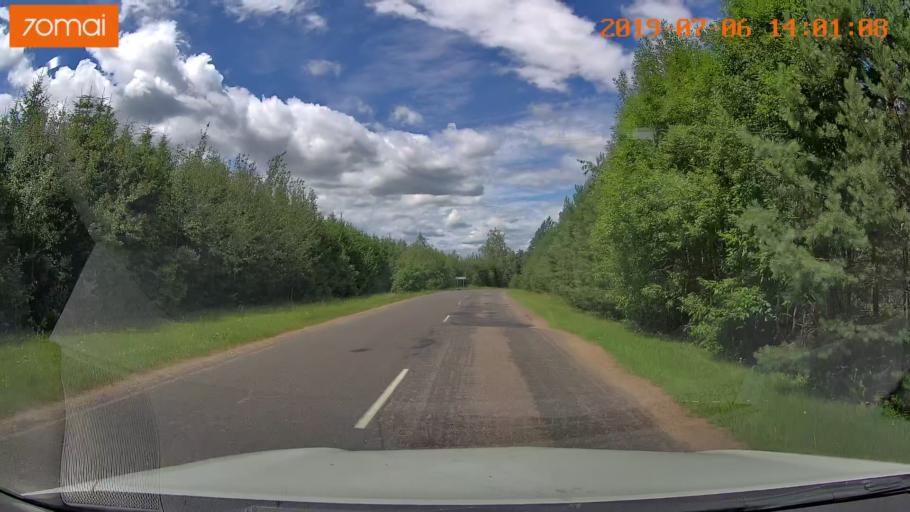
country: BY
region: Minsk
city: Ivyanyets
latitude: 53.8050
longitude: 26.8154
